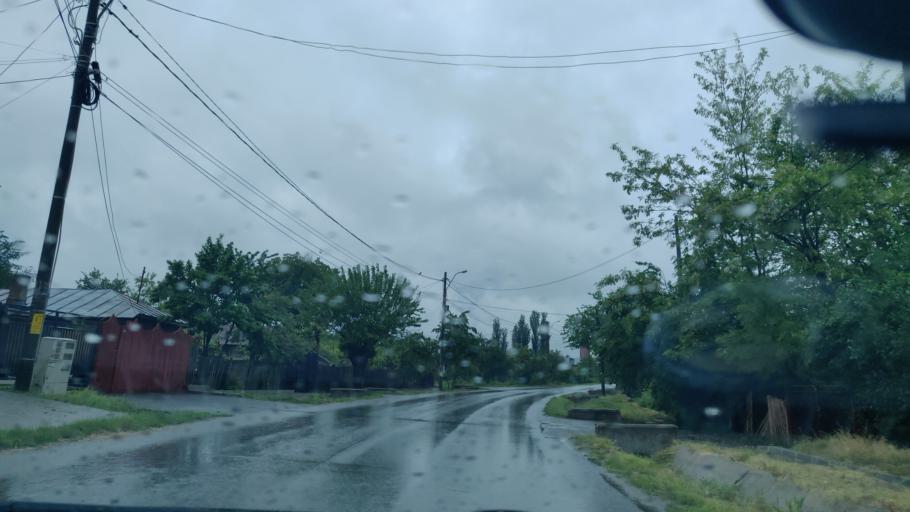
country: RO
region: Giurgiu
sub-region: Comuna Bulbucata
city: Bulbucata
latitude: 44.2808
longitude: 25.8135
